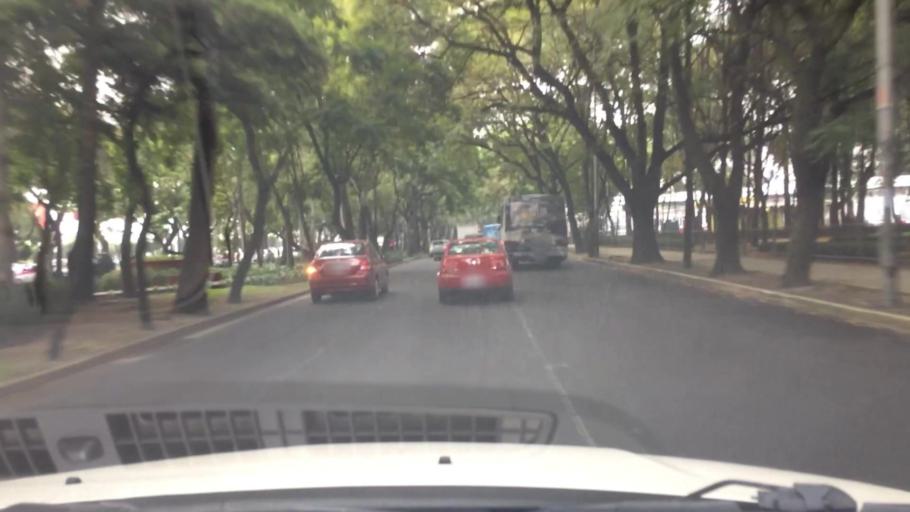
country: MX
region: Mexico City
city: Coyoacan
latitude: 19.3224
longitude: -99.1340
